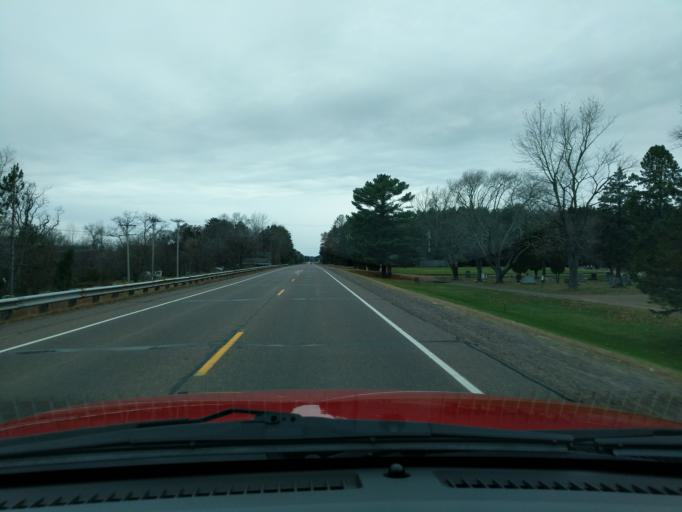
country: US
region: Wisconsin
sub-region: Washburn County
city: Spooner
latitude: 45.8216
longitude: -91.9063
